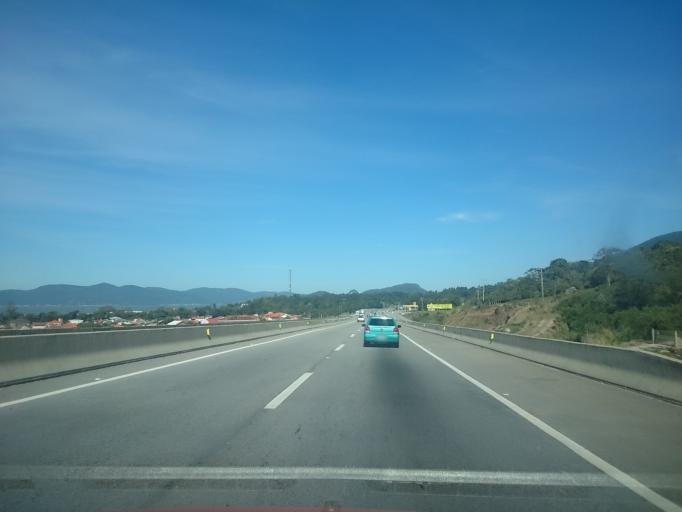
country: BR
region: Santa Catarina
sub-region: Palhoca
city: Palhoca
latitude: -27.7173
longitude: -48.6478
